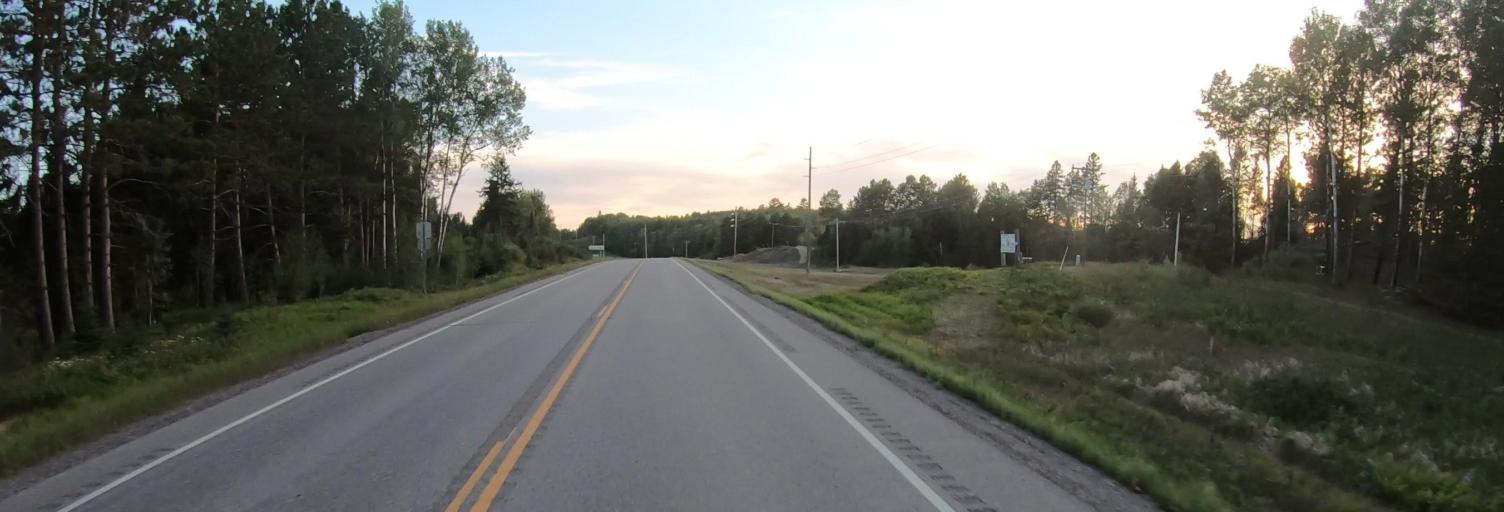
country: US
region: Minnesota
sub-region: Saint Louis County
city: Ely
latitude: 47.8807
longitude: -92.0077
